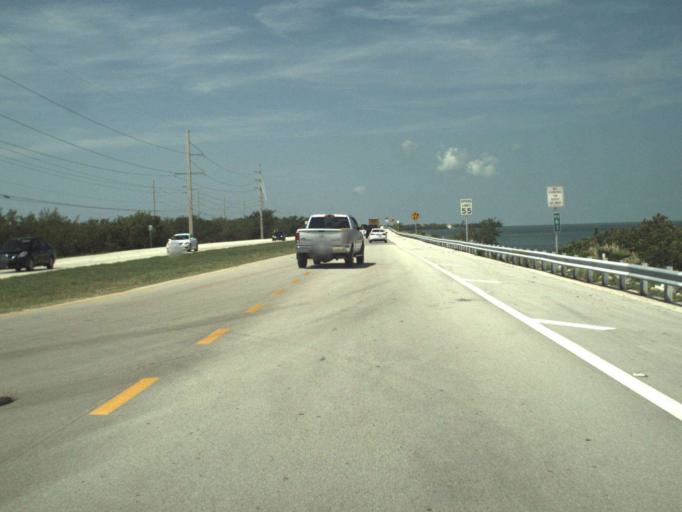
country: US
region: Florida
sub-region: Monroe County
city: Marathon
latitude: 24.7800
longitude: -80.9155
